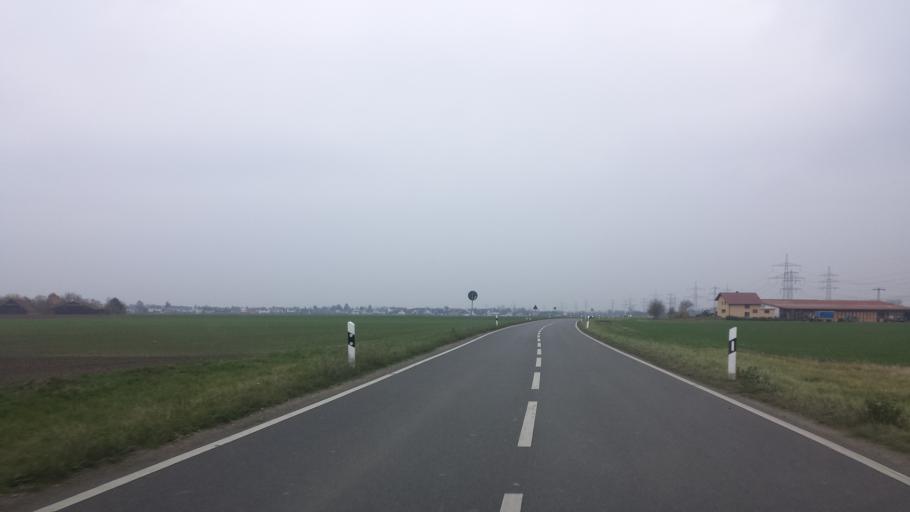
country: DE
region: Rheinland-Pfalz
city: Worms
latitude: 49.6686
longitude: 8.3895
